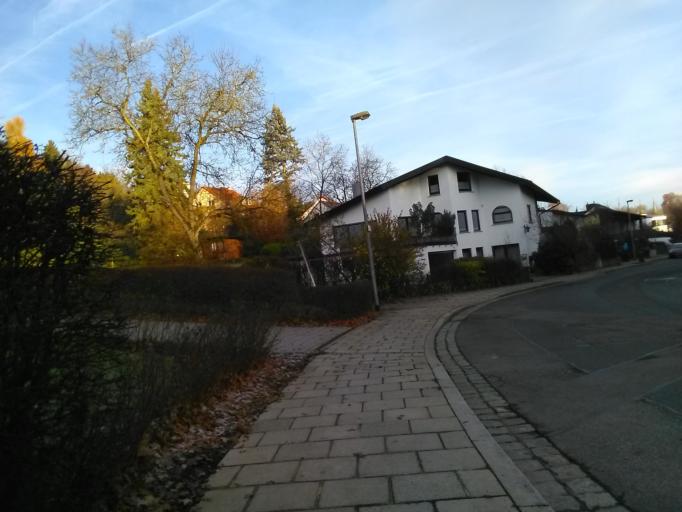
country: DE
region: Bavaria
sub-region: Upper Franconia
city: Bamberg
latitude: 49.8822
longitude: 10.8785
